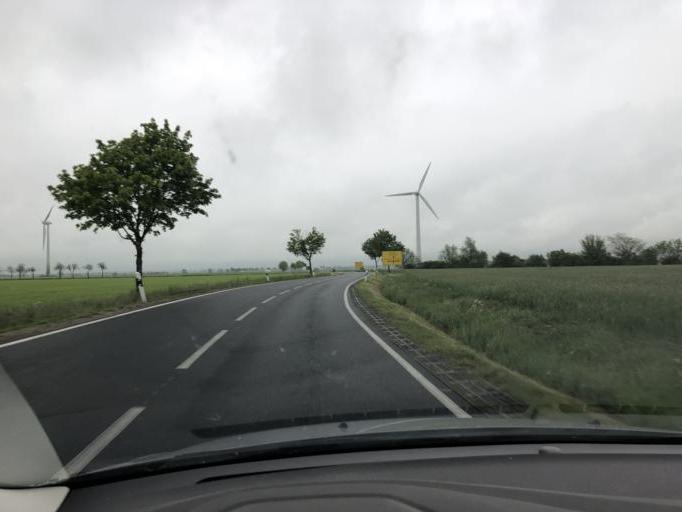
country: DE
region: Saxony
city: Zschortau
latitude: 51.5045
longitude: 12.3821
